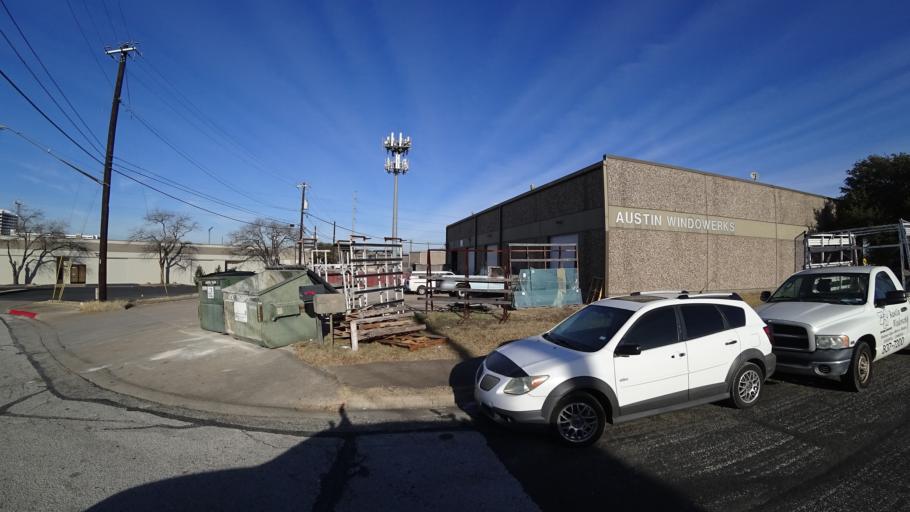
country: US
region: Texas
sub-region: Travis County
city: Wells Branch
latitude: 30.3920
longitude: -97.7154
